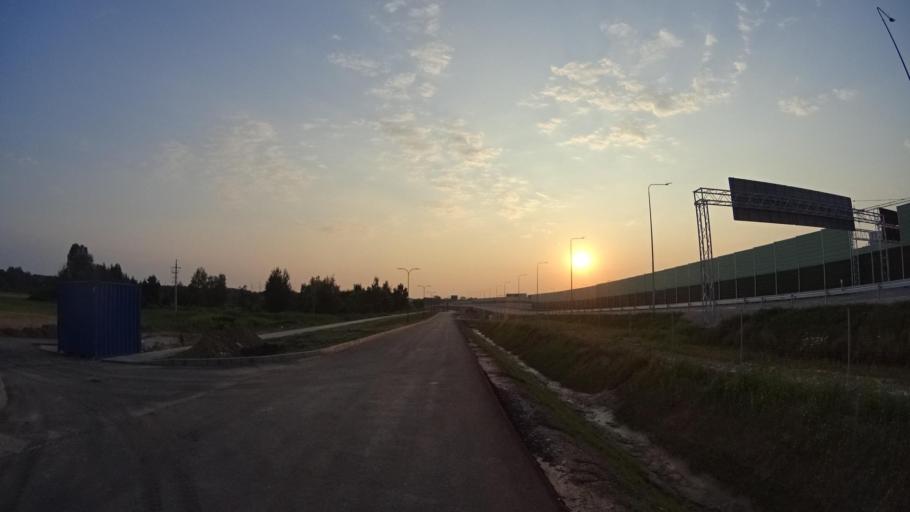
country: PL
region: Masovian Voivodeship
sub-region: Warszawa
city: Wilanow
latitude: 52.1522
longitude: 21.0809
